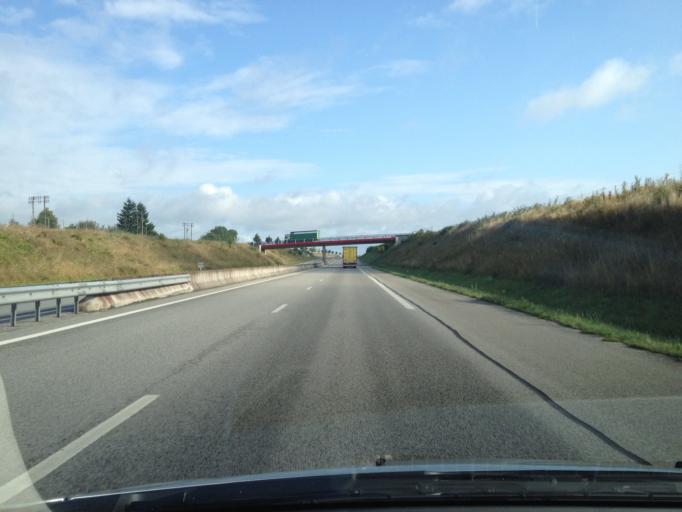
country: FR
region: Lower Normandy
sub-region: Departement de l'Orne
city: Sees
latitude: 48.5618
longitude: 0.1761
